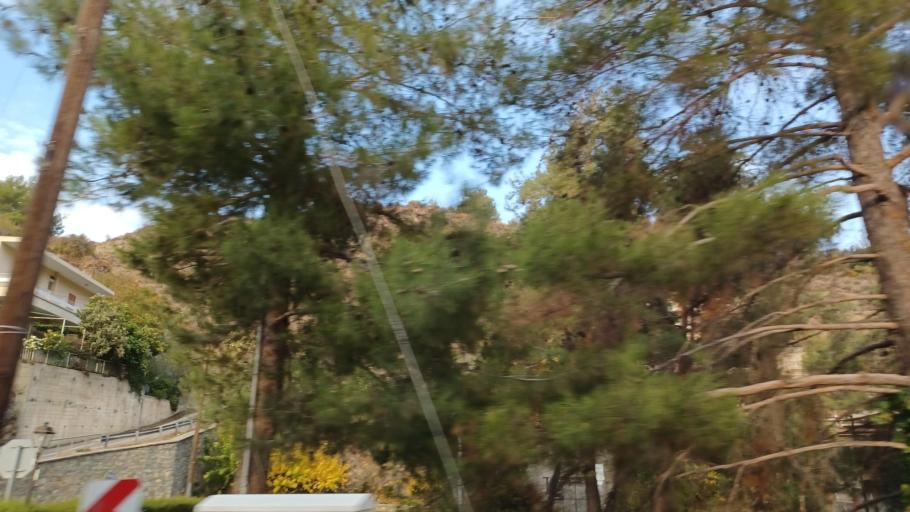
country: CY
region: Lefkosia
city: Kakopetria
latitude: 34.9909
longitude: 32.9069
